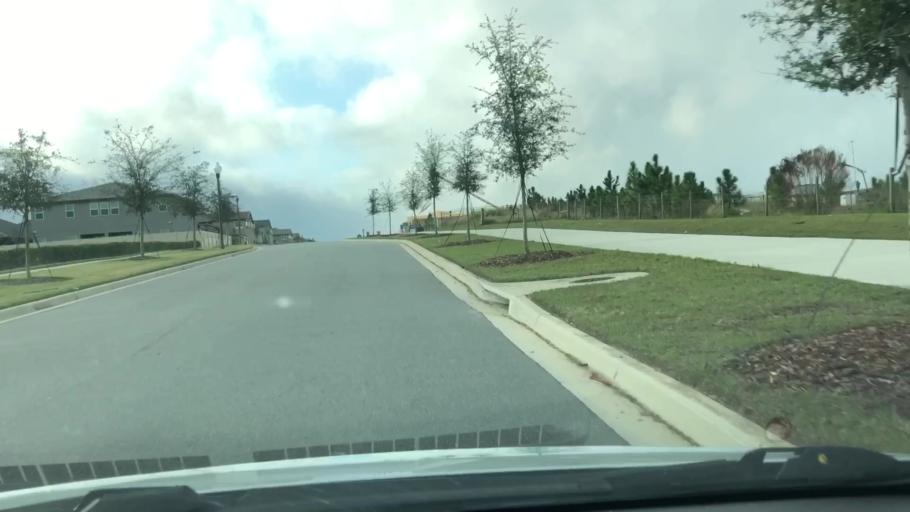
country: US
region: Florida
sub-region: Polk County
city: Citrus Ridge
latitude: 28.4350
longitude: -81.6238
